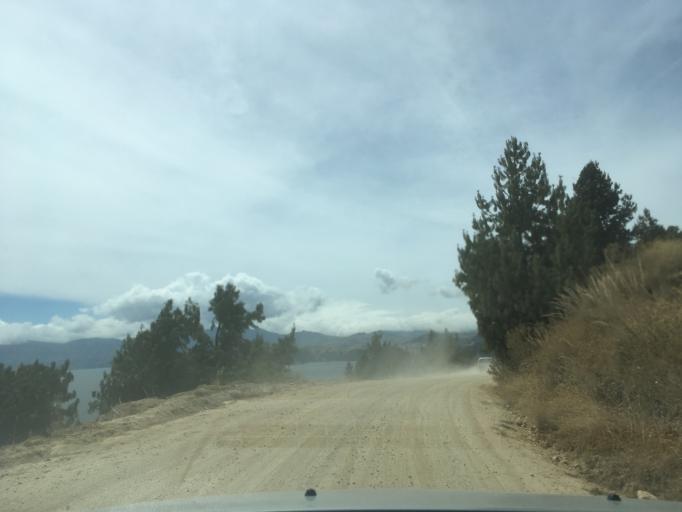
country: CO
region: Boyaca
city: Aquitania
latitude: 5.5803
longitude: -72.9275
